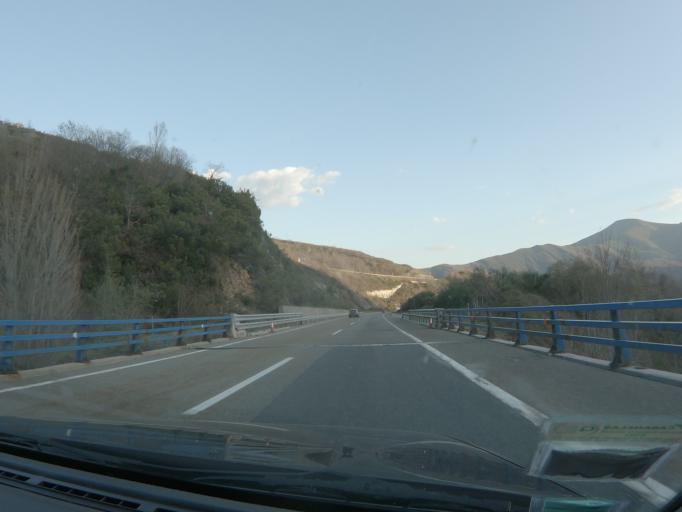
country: ES
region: Castille and Leon
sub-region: Provincia de Leon
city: Vega de Valcarce
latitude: 42.6892
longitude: -6.9904
